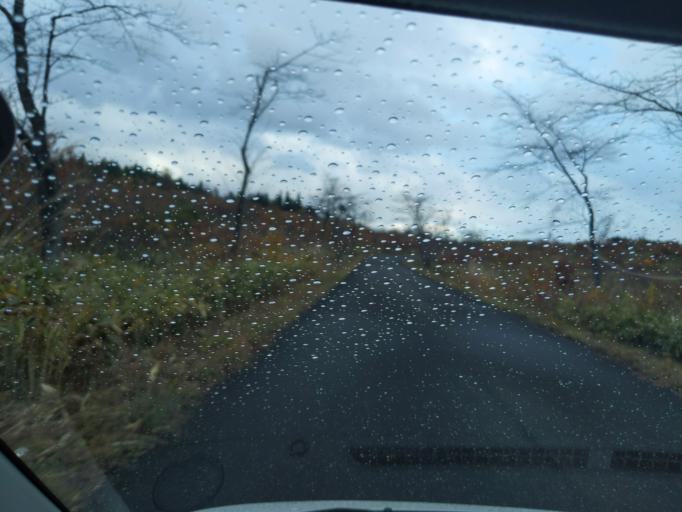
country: JP
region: Iwate
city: Mizusawa
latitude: 39.0857
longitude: 141.0127
